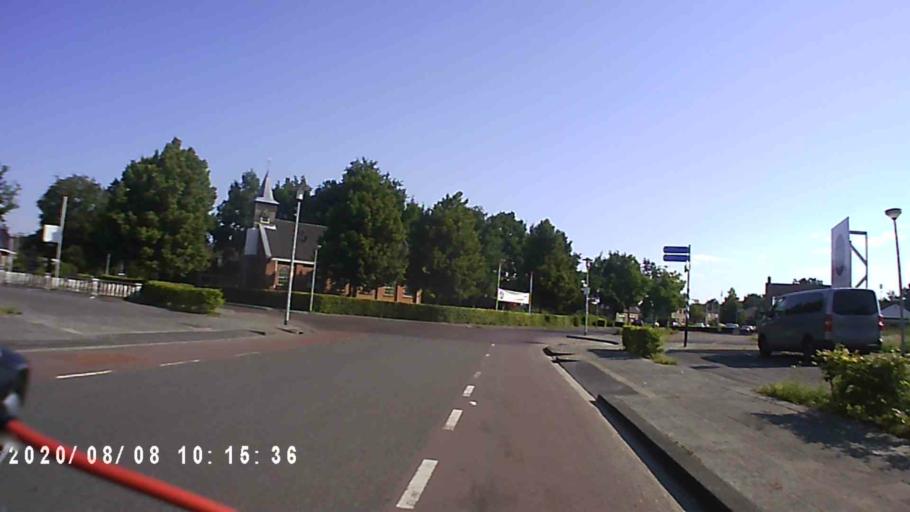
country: NL
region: Groningen
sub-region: Gemeente Leek
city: Leek
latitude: 53.1308
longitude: 6.3976
